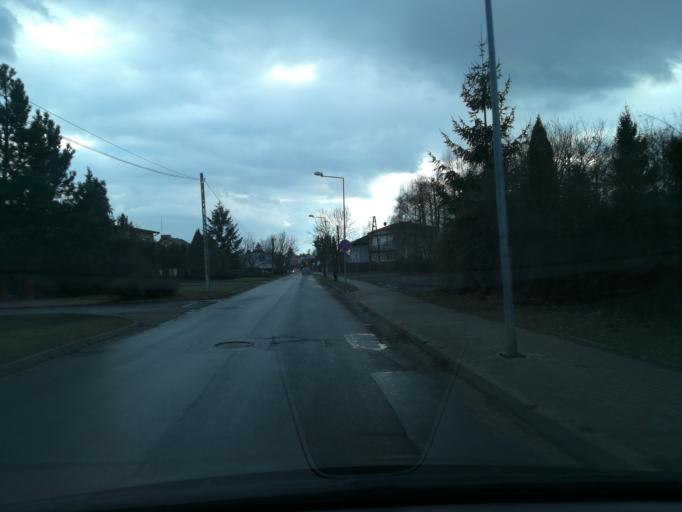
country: PL
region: Lodz Voivodeship
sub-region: Powiat radomszczanski
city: Radomsko
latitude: 51.0698
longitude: 19.4235
